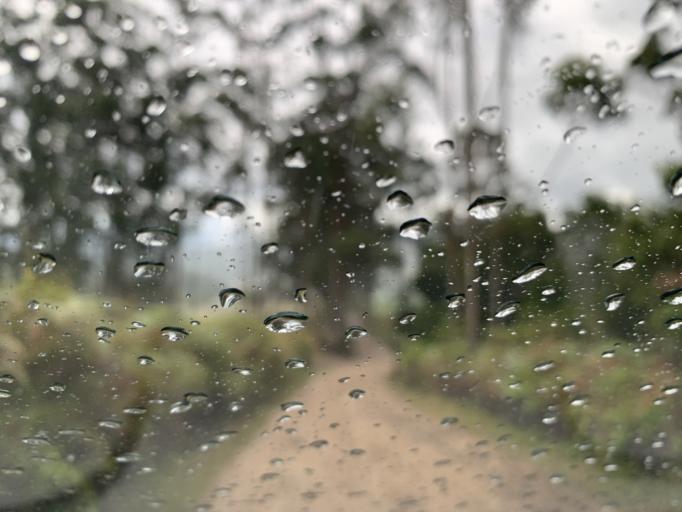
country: CO
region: Boyaca
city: Arcabuco
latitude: 5.7514
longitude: -73.4697
